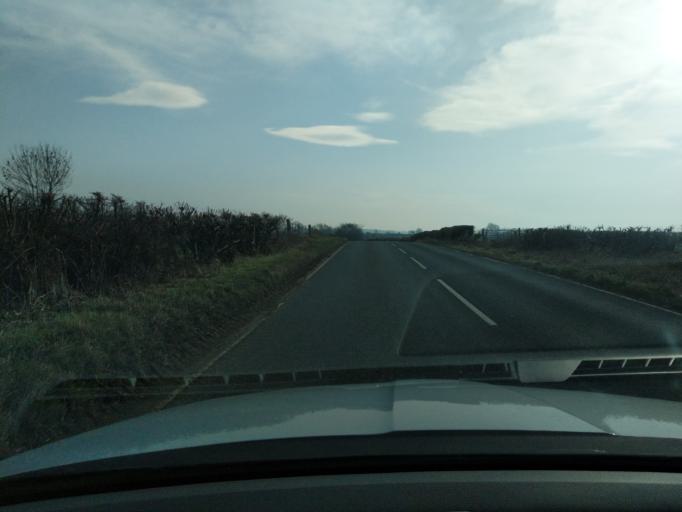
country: GB
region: England
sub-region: North Yorkshire
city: Catterick Garrison
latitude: 54.3293
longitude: -1.6852
